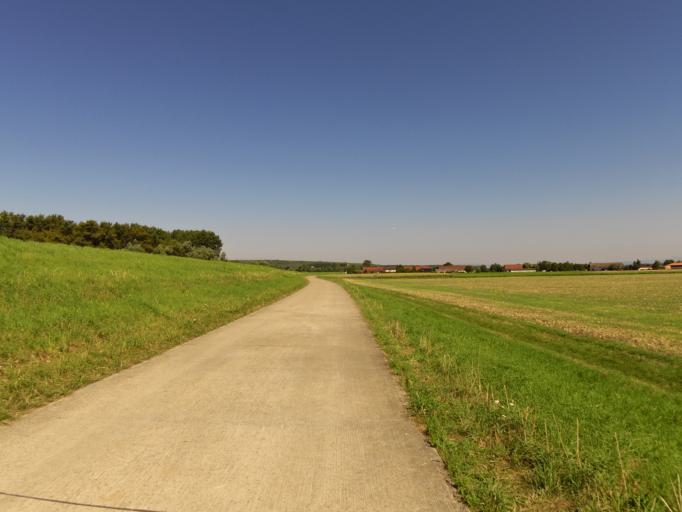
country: DE
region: Rheinland-Pfalz
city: Nierstein
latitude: 49.8836
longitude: 8.3625
